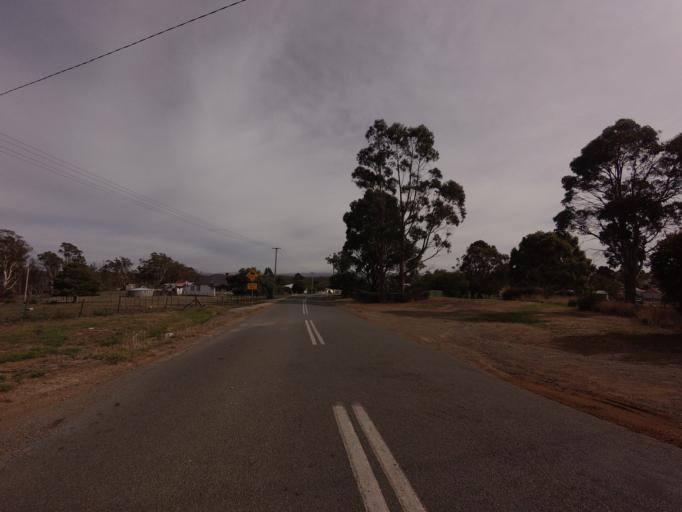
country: AU
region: Tasmania
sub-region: Brighton
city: Bridgewater
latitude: -42.3580
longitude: 147.4076
